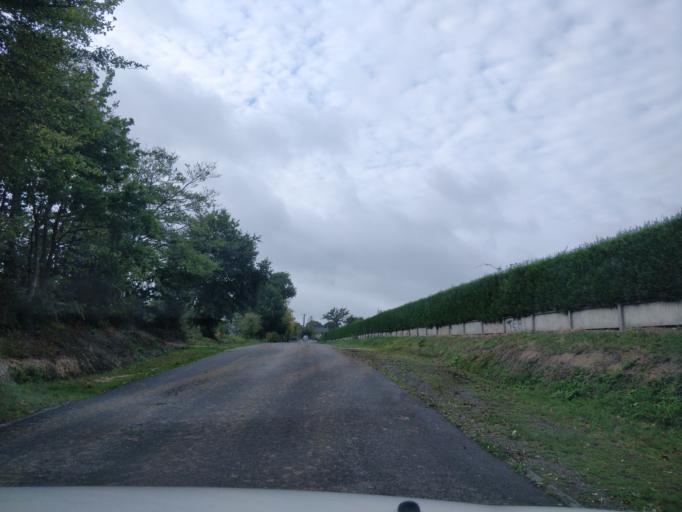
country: FR
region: Brittany
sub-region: Departement d'Ille-et-Vilaine
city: La Bouexiere
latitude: 48.1805
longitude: -1.4319
